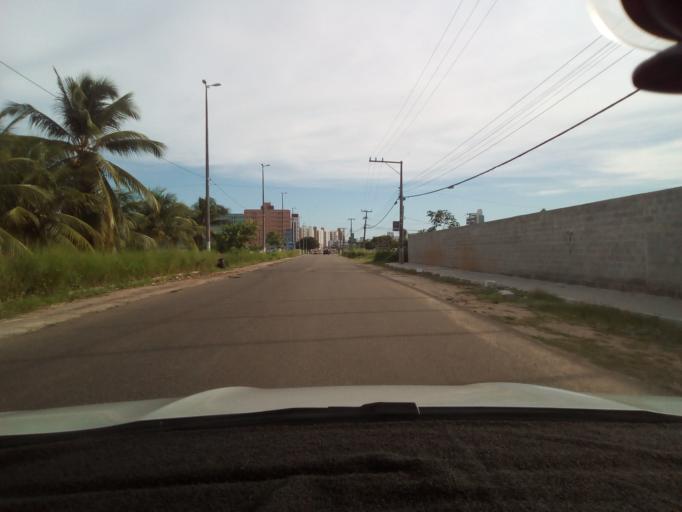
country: BR
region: Paraiba
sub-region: Cabedelo
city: Cabedelo
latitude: -7.0268
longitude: -34.8310
